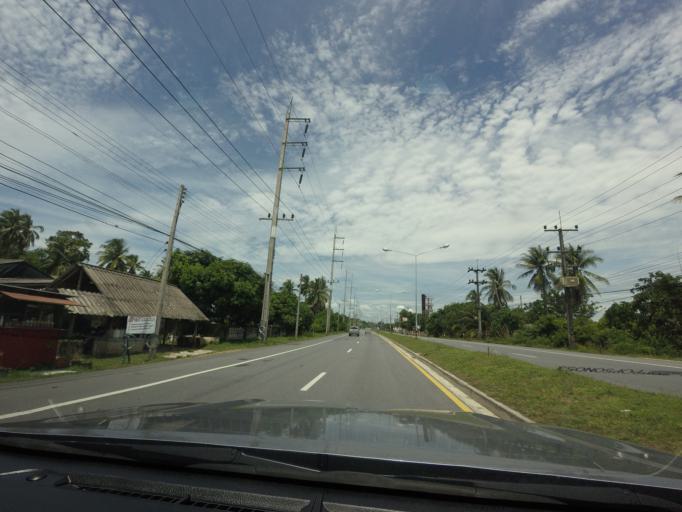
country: TH
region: Songkhla
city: Krasae Sin
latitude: 7.5809
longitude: 100.4073
